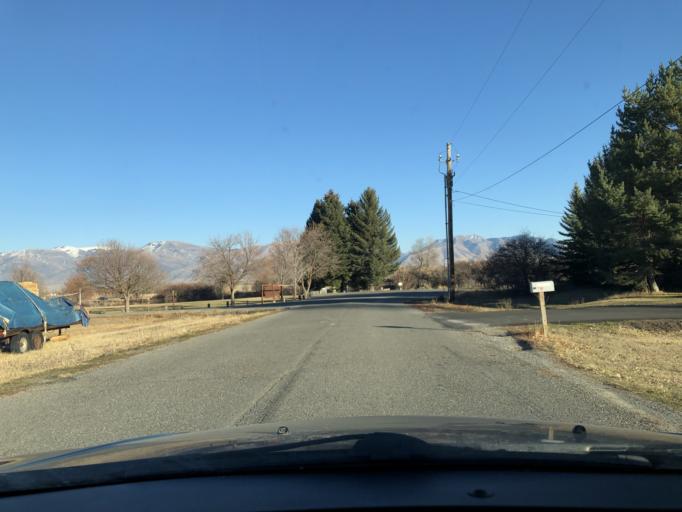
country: US
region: Utah
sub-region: Cache County
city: Wellsville
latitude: 41.6283
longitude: -111.9327
